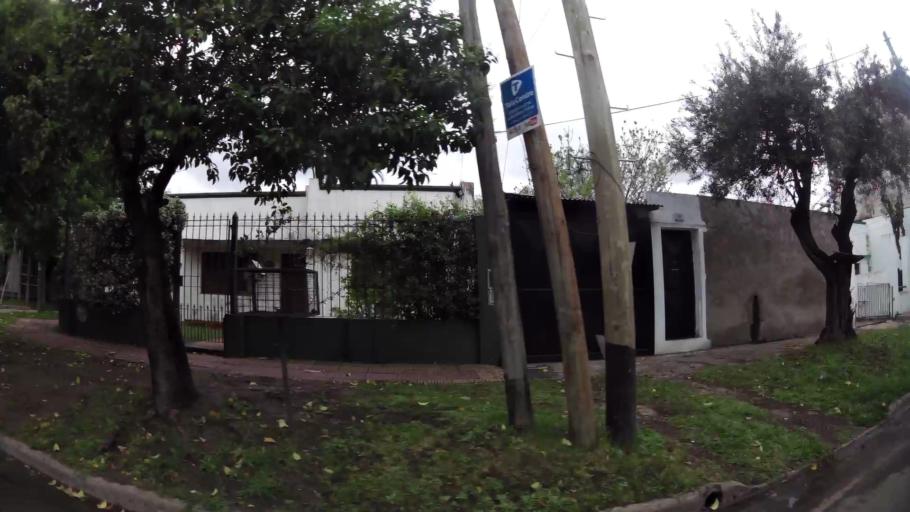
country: AR
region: Buenos Aires
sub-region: Partido de Lanus
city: Lanus
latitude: -34.7345
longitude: -58.3835
